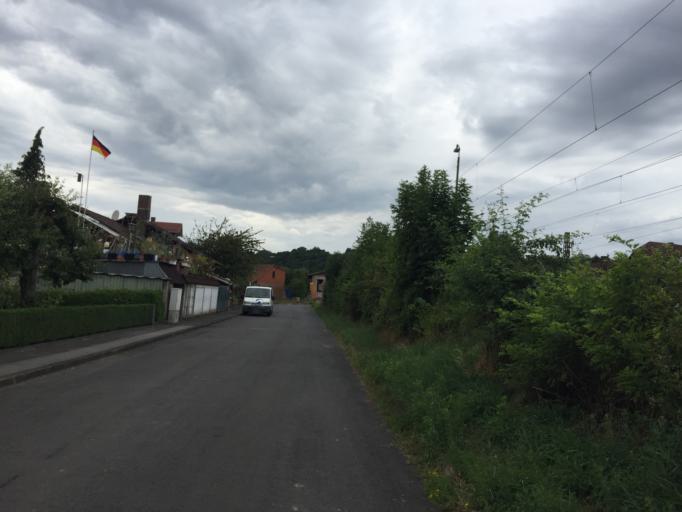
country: DE
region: Hesse
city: Bebra
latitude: 50.9895
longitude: 9.7679
